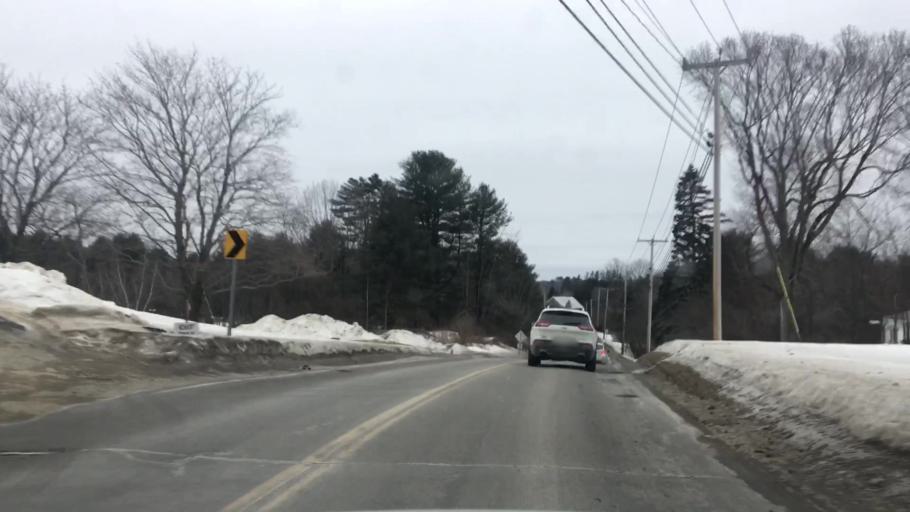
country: US
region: Maine
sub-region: Androscoggin County
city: Auburn
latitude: 44.1218
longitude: -70.2548
